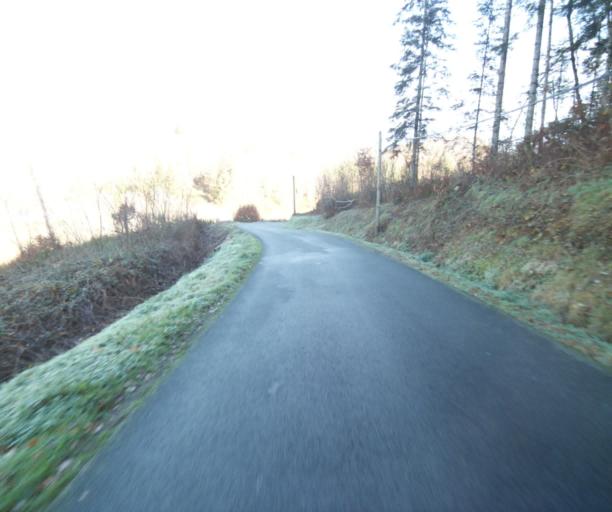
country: FR
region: Limousin
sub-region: Departement de la Correze
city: Chameyrat
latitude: 45.2337
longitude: 1.7315
